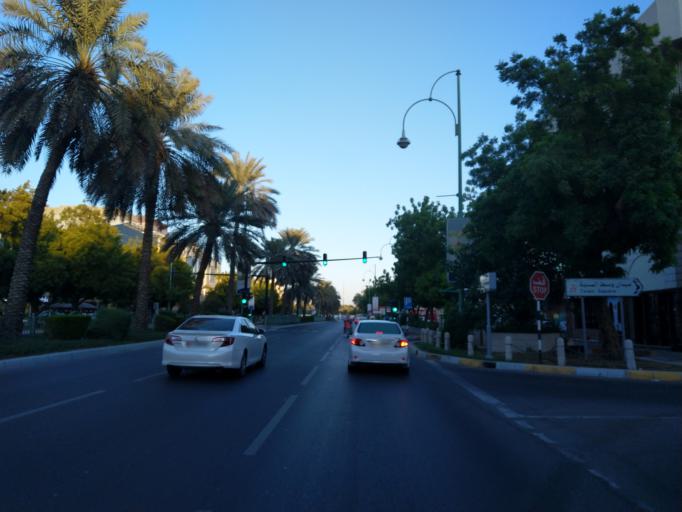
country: AE
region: Abu Dhabi
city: Al Ain
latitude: 24.2253
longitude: 55.7671
